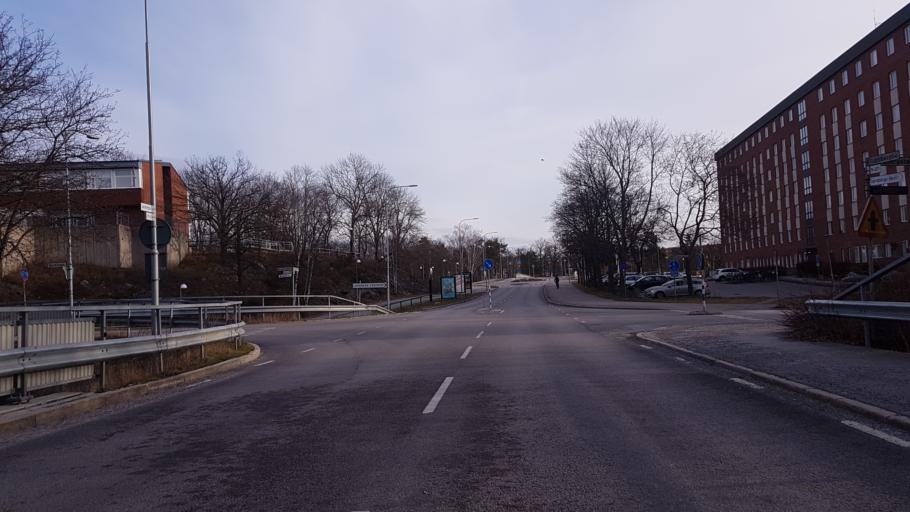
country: SE
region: Stockholm
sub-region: Lidingo
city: Lidingoe
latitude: 59.3492
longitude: 18.1426
